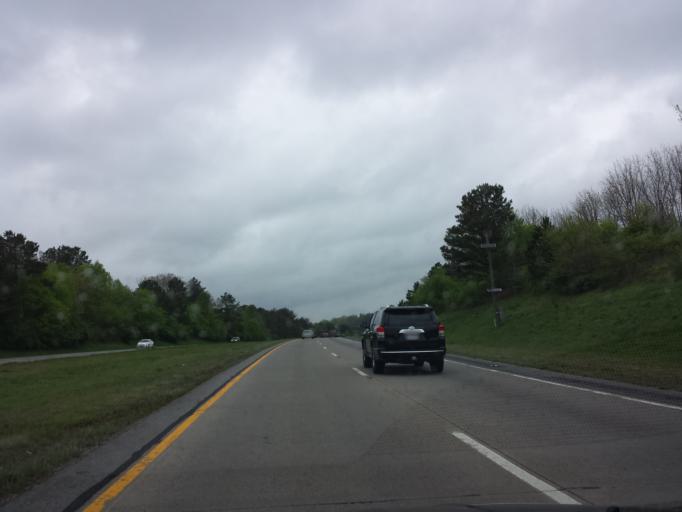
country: US
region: Georgia
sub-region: Pickens County
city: Jasper
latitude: 34.4098
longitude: -84.4249
